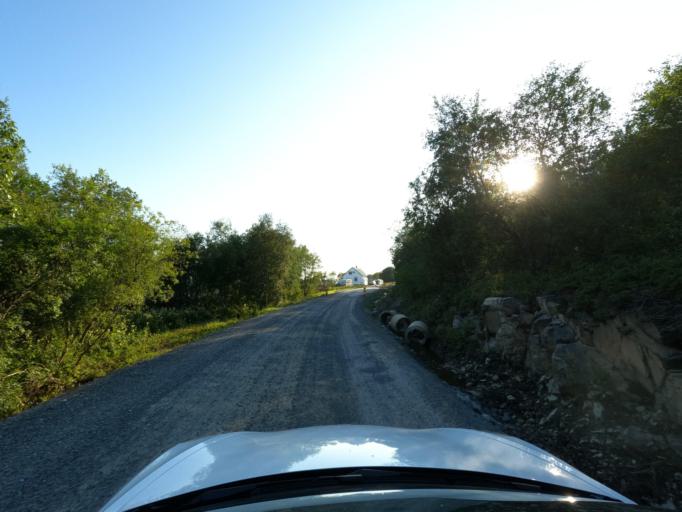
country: NO
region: Nordland
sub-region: Ballangen
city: Ballangen
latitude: 68.4584
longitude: 16.7055
